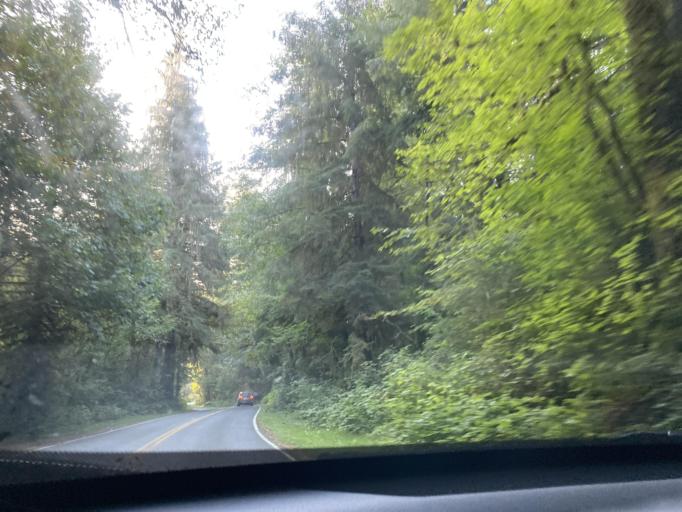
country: US
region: Washington
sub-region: Clallam County
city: Forks
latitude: 47.8188
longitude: -124.1745
